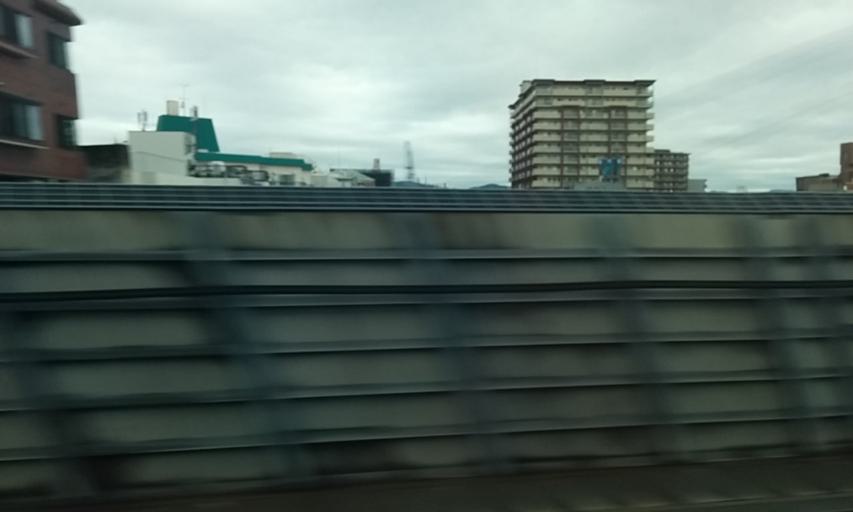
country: JP
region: Hyogo
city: Takarazuka
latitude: 34.7646
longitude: 135.3594
